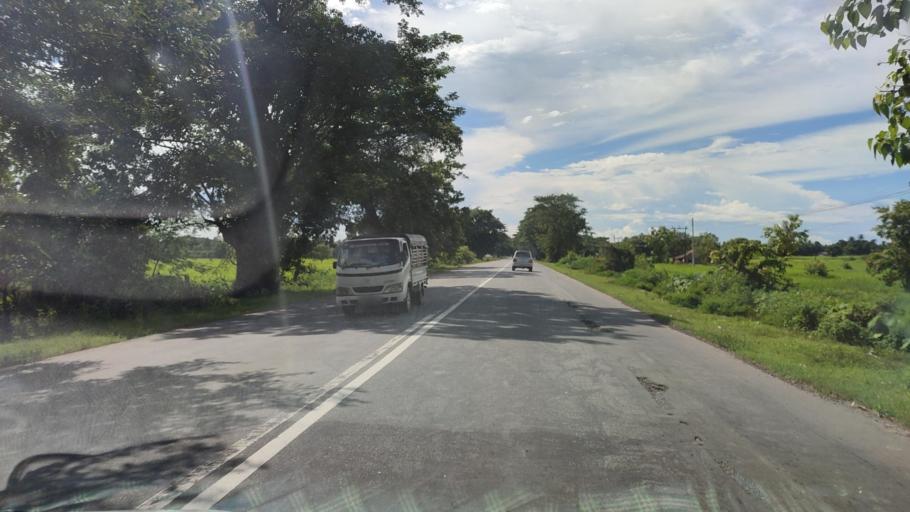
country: MM
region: Bago
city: Pyu
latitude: 18.2362
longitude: 96.5509
